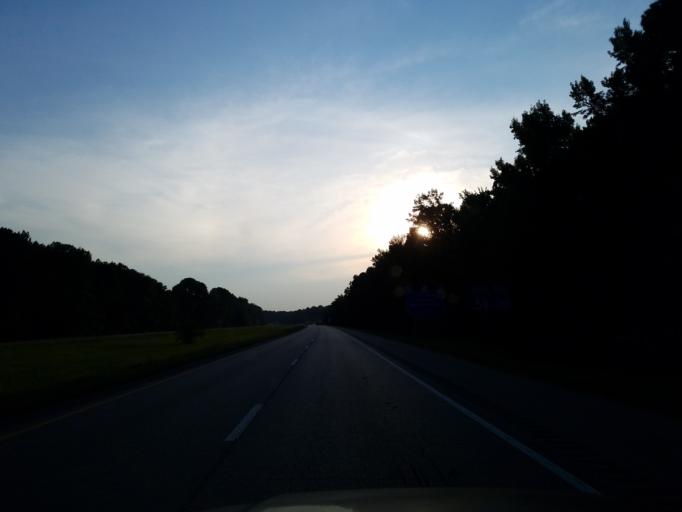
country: US
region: Mississippi
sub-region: Lauderdale County
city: Marion
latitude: 32.4137
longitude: -88.5129
